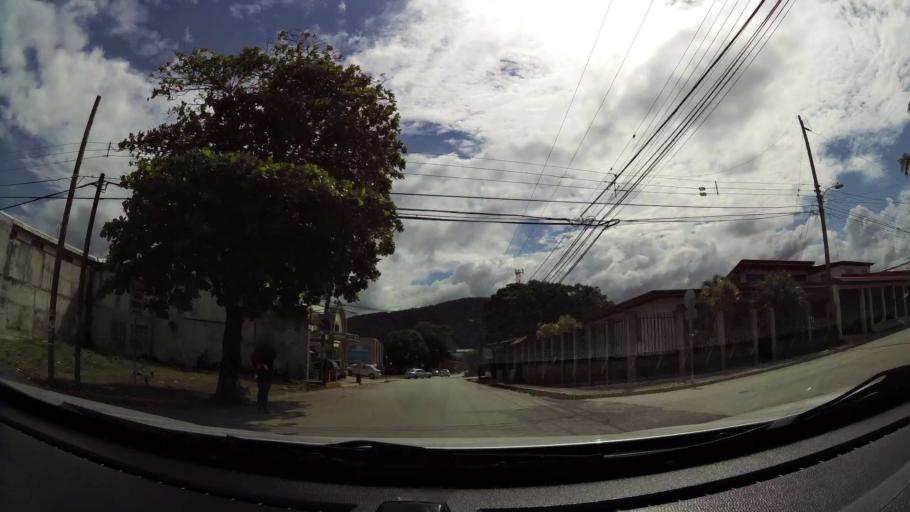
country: CR
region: Guanacaste
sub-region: Canton de Nicoya
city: Nicoya
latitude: 10.1464
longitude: -85.4529
